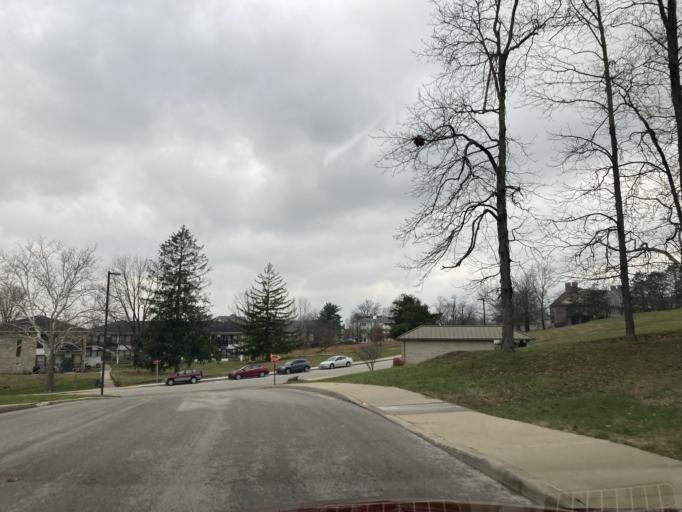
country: US
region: Indiana
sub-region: Monroe County
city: Bloomington
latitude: 39.1768
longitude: -86.5093
